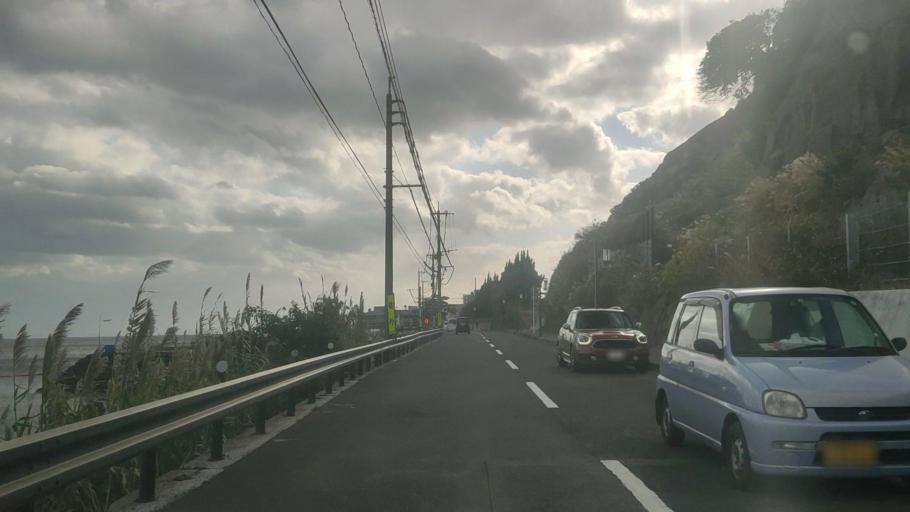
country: JP
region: Kagoshima
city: Kagoshima-shi
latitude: 31.6109
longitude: 130.5749
